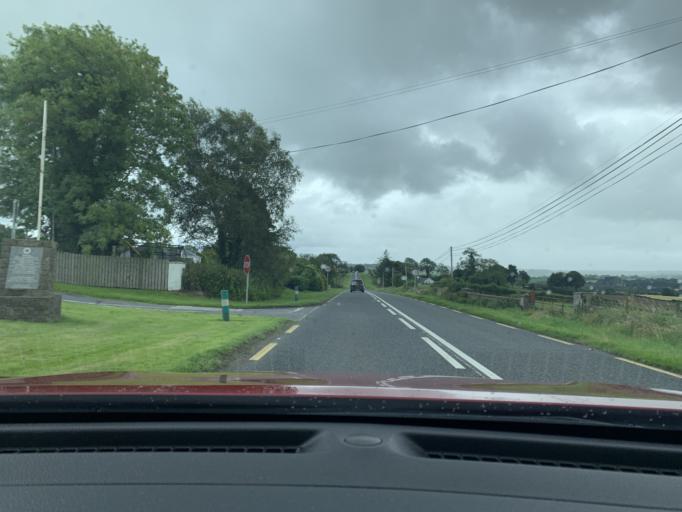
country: IE
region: Ulster
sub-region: County Donegal
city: Raphoe
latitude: 54.7999
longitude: -7.5753
